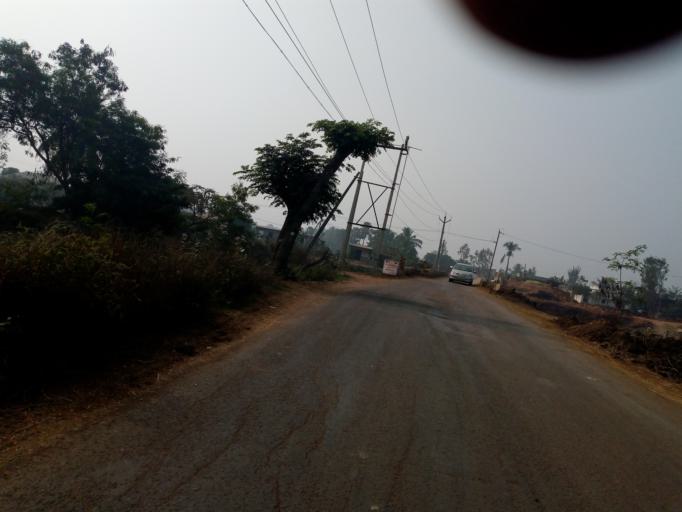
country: IN
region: Andhra Pradesh
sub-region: West Godavari
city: Tadepallegudem
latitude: 16.7461
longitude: 81.4204
